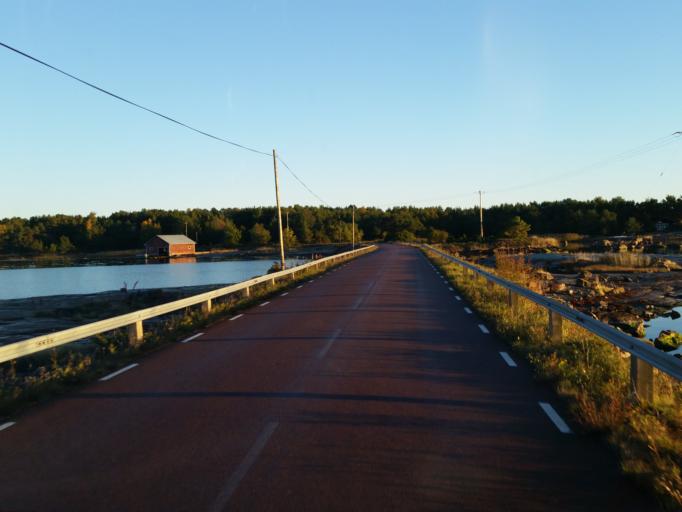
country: AX
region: Alands skaergard
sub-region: Vardoe
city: Vardoe
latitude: 60.3337
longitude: 20.3652
